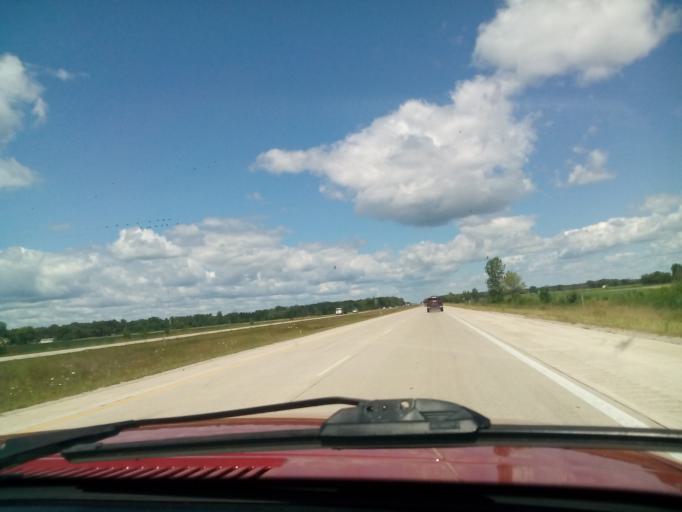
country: US
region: Michigan
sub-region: Bay County
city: Pinconning
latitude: 43.8108
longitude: -84.0205
